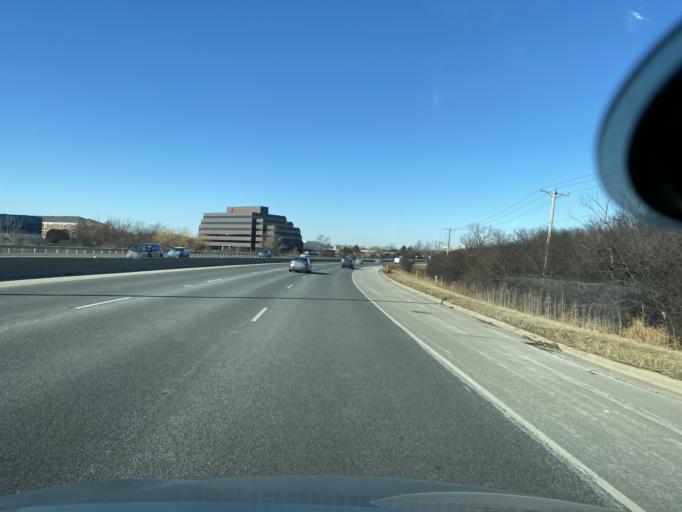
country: US
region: Illinois
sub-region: DuPage County
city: Clarendon Hills
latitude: 41.8160
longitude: -87.9510
